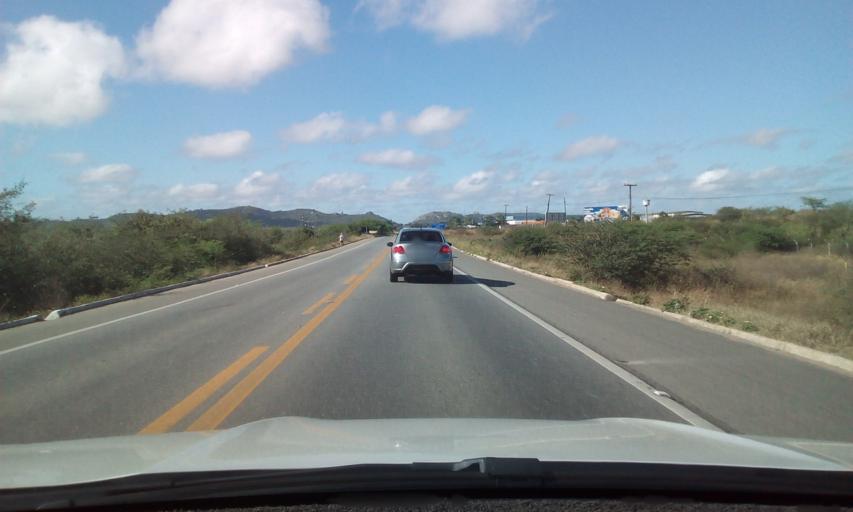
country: BR
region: Paraiba
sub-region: Campina Grande
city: Campina Grande
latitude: -7.3100
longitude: -35.8939
